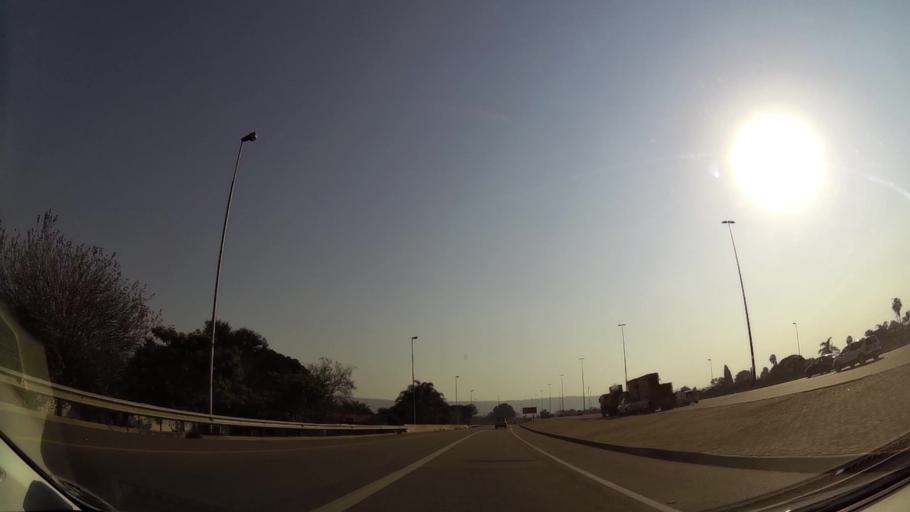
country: ZA
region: Gauteng
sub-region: City of Tshwane Metropolitan Municipality
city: Pretoria
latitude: -25.7157
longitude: 28.2652
